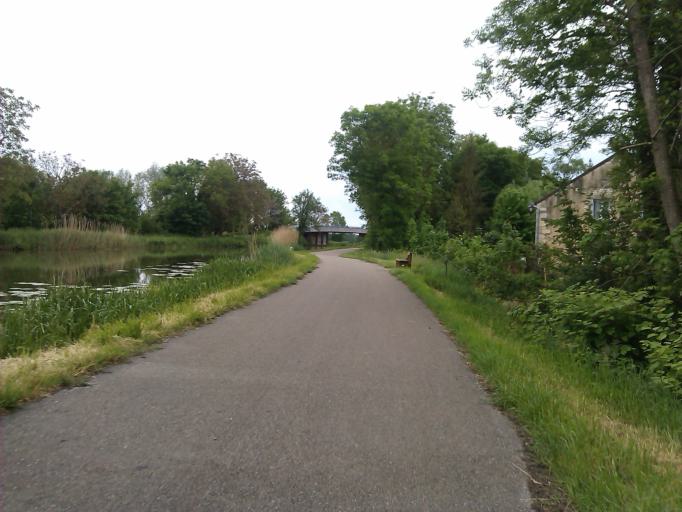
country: FR
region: Franche-Comte
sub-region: Departement du Jura
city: Choisey
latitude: 47.0626
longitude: 5.4621
